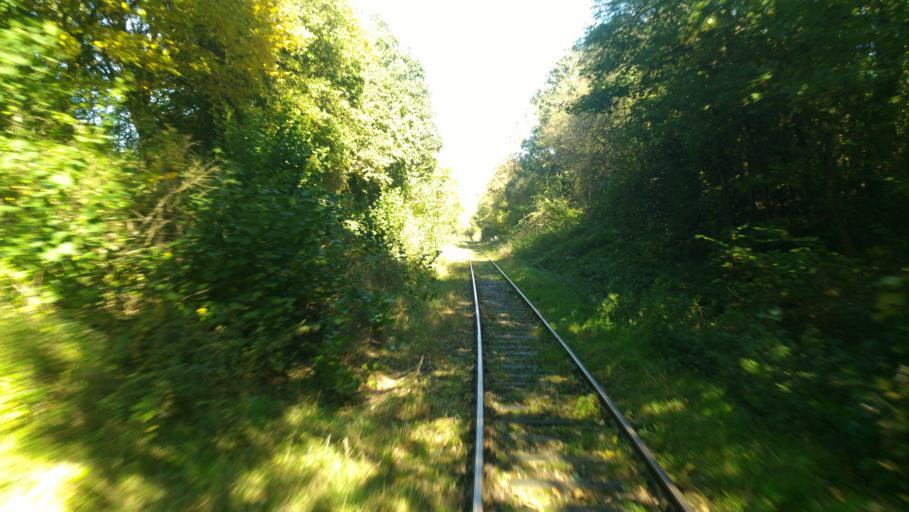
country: DE
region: Lower Saxony
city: Obernkirchen
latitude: 52.2624
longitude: 9.1278
